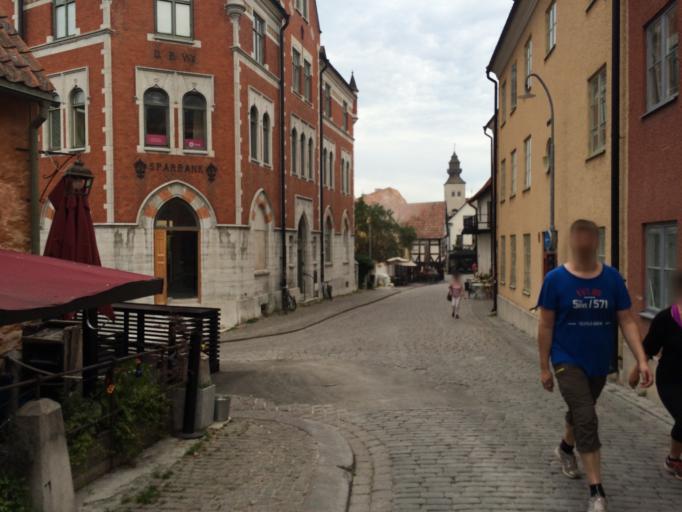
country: SE
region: Gotland
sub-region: Gotland
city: Visby
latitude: 57.6392
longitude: 18.2961
